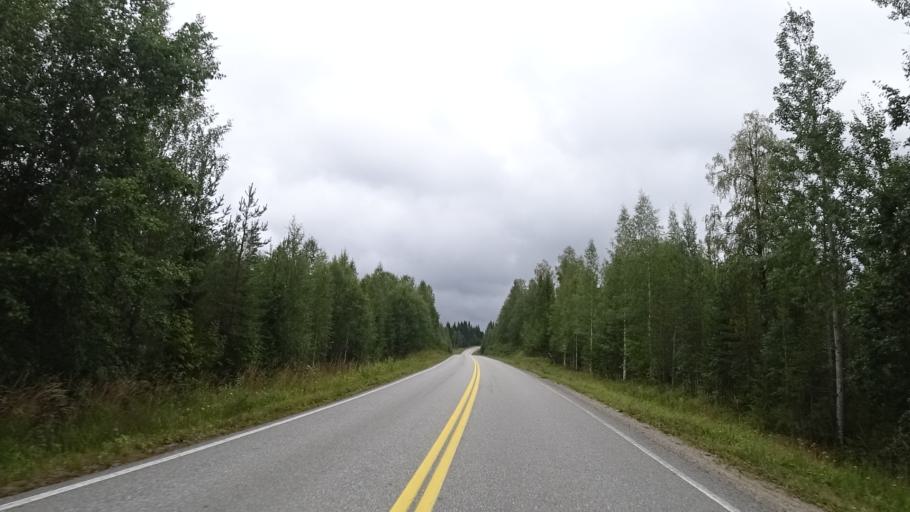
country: FI
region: North Karelia
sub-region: Joensuu
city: Ilomantsi
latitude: 63.2597
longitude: 30.6706
